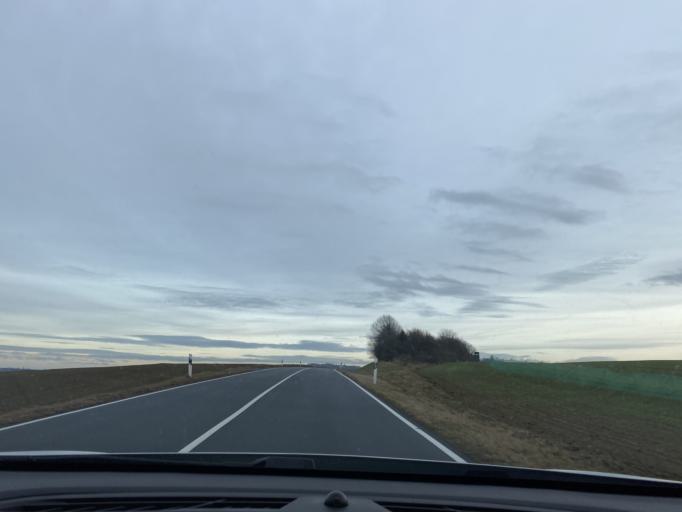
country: DE
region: Saxony
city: Markersdorf
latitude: 51.1090
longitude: 14.8641
